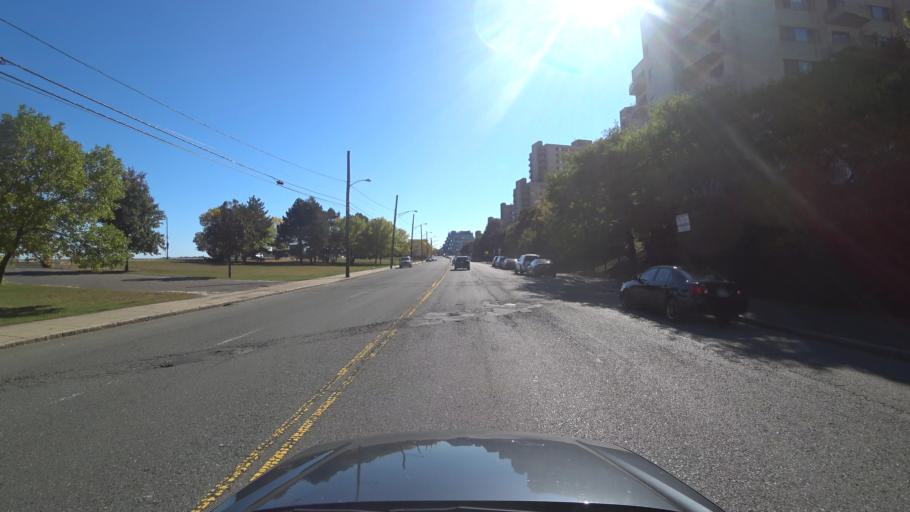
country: US
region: Massachusetts
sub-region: Suffolk County
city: Revere
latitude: 42.4116
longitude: -70.9910
